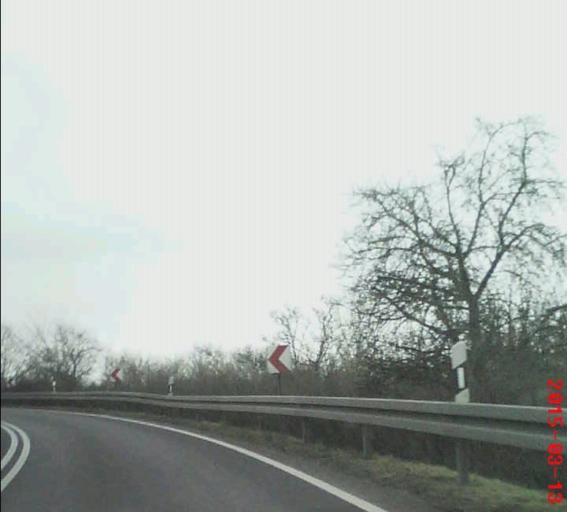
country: DE
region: Thuringia
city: Andisleben
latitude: 51.0808
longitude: 10.9240
